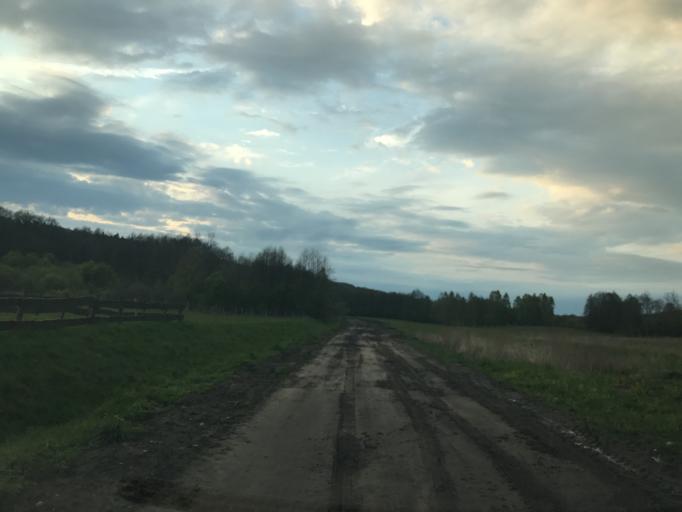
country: PL
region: Warmian-Masurian Voivodeship
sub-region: Powiat ilawski
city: Lubawa
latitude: 53.5368
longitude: 19.8946
